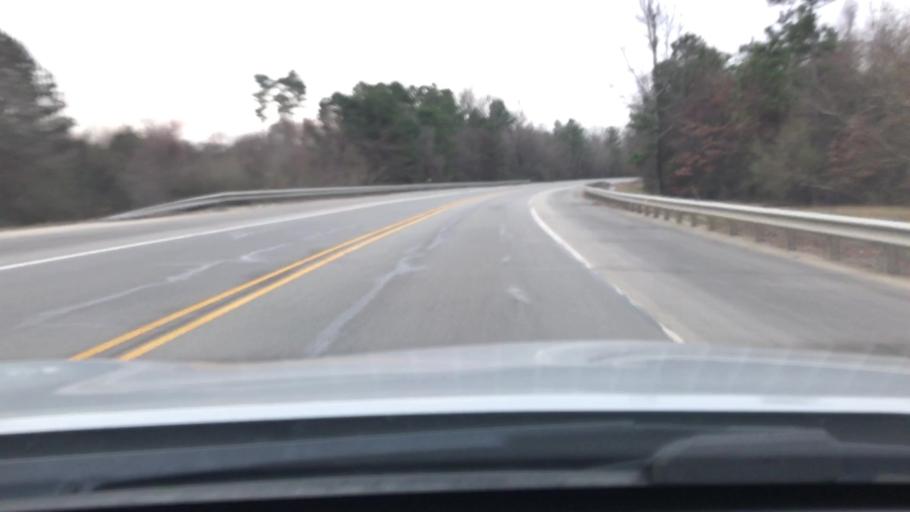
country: US
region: Arkansas
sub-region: Hempstead County
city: Hope
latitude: 33.6836
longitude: -93.5760
